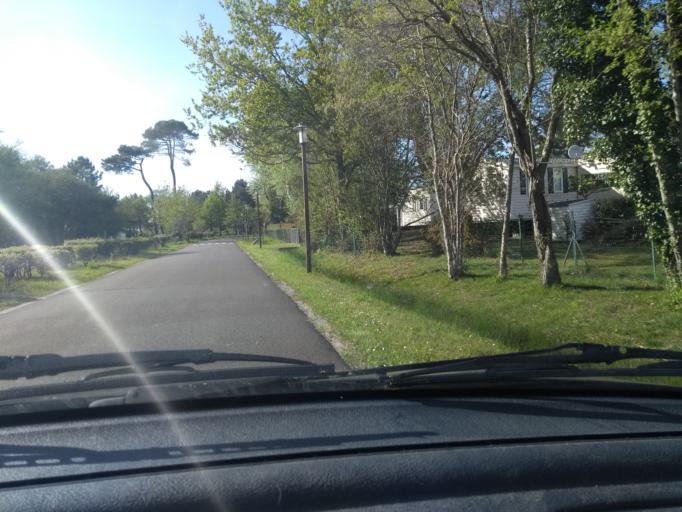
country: FR
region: Aquitaine
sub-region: Departement des Landes
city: Parentis-en-Born
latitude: 44.3448
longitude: -1.0997
